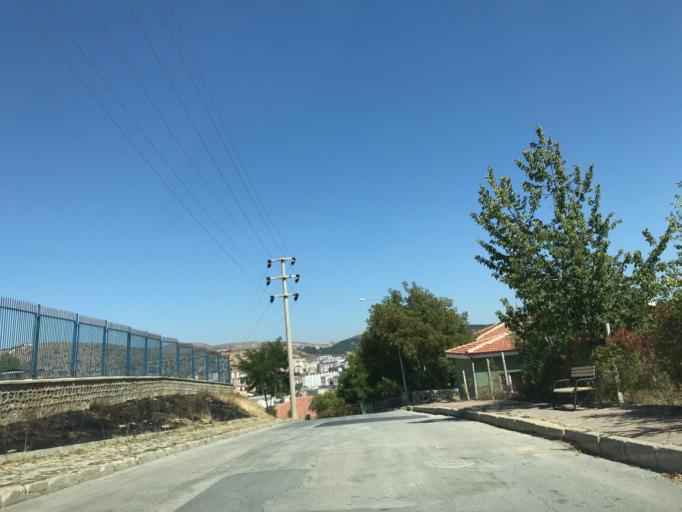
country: TR
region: Yozgat
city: Yozgat
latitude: 39.8146
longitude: 34.8227
